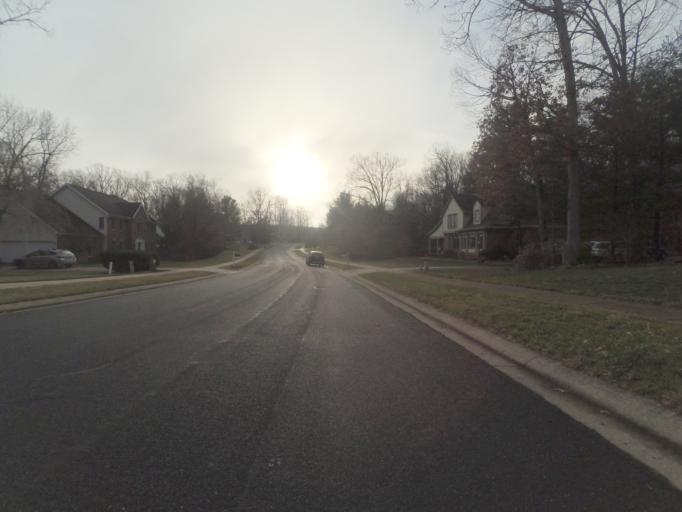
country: US
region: Pennsylvania
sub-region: Centre County
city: Park Forest Village
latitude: 40.7911
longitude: -77.9143
